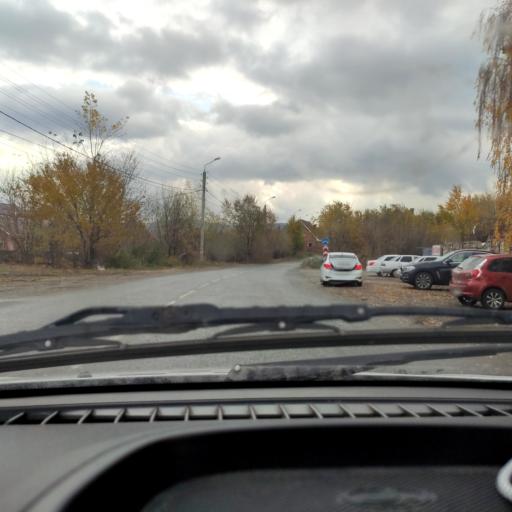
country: RU
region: Samara
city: Zhigulevsk
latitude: 53.4661
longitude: 49.6206
